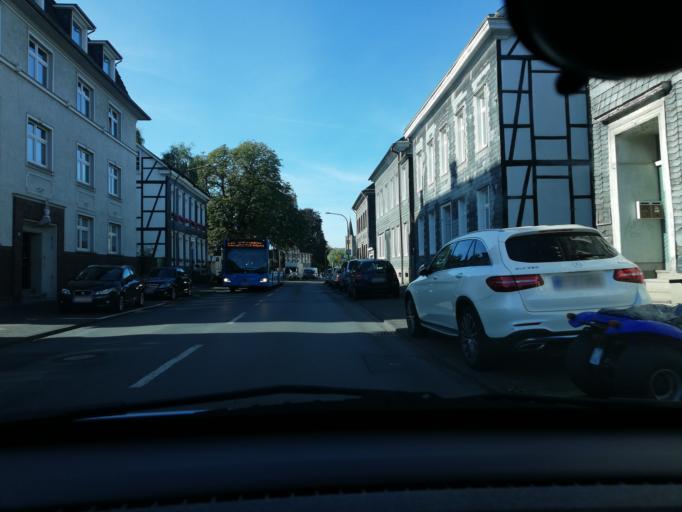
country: DE
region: North Rhine-Westphalia
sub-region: Regierungsbezirk Dusseldorf
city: Wuppertal
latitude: 51.2842
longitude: 7.2183
